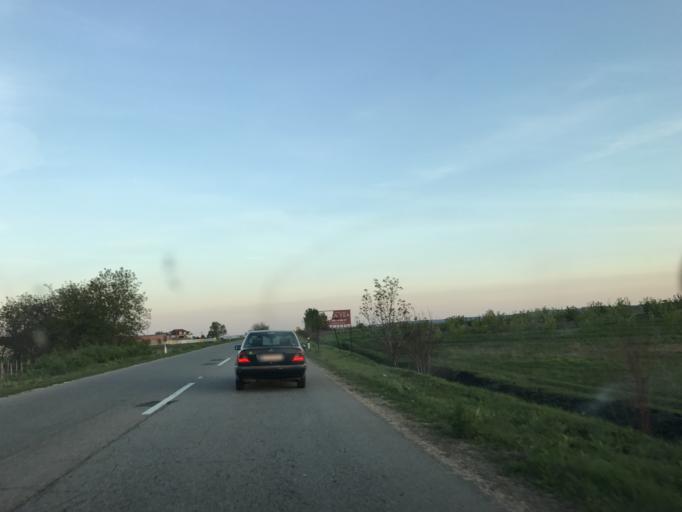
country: RS
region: Central Serbia
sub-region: Borski Okrug
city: Negotin
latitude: 44.2651
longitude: 22.5158
